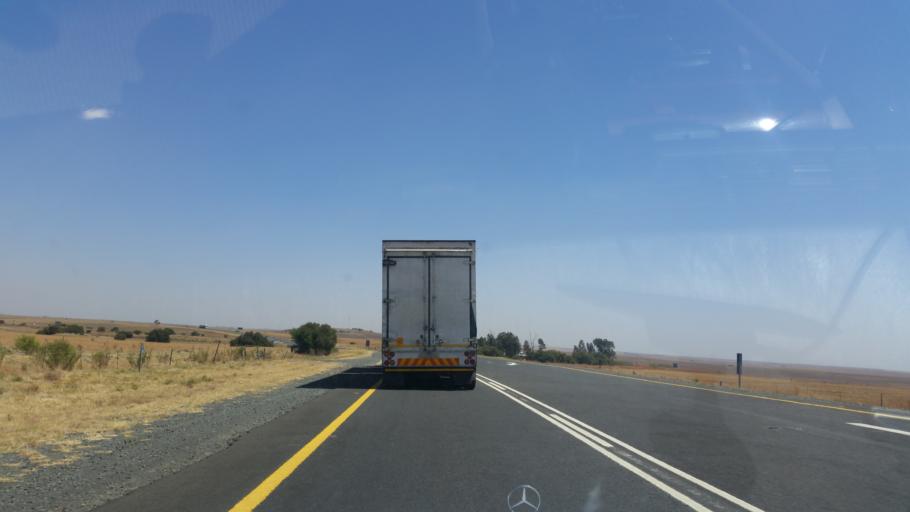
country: ZA
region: Orange Free State
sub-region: Lejweleputswa District Municipality
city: Winburg
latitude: -28.4953
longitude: 27.0401
